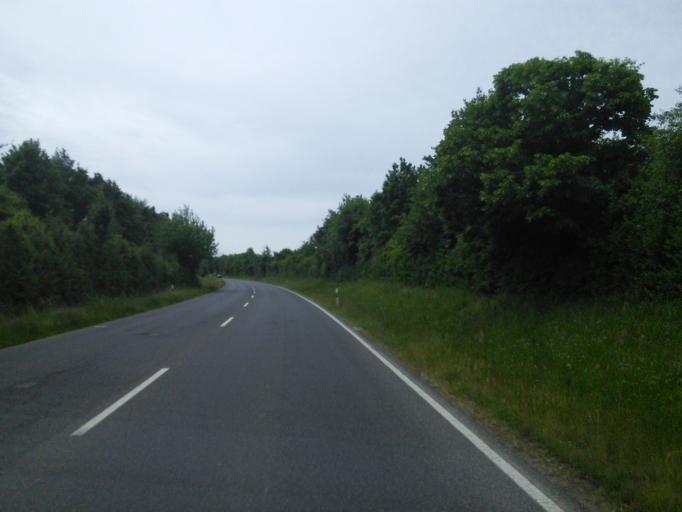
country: DE
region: North Rhine-Westphalia
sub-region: Regierungsbezirk Koln
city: Rheinbach
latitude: 50.6290
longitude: 6.9303
